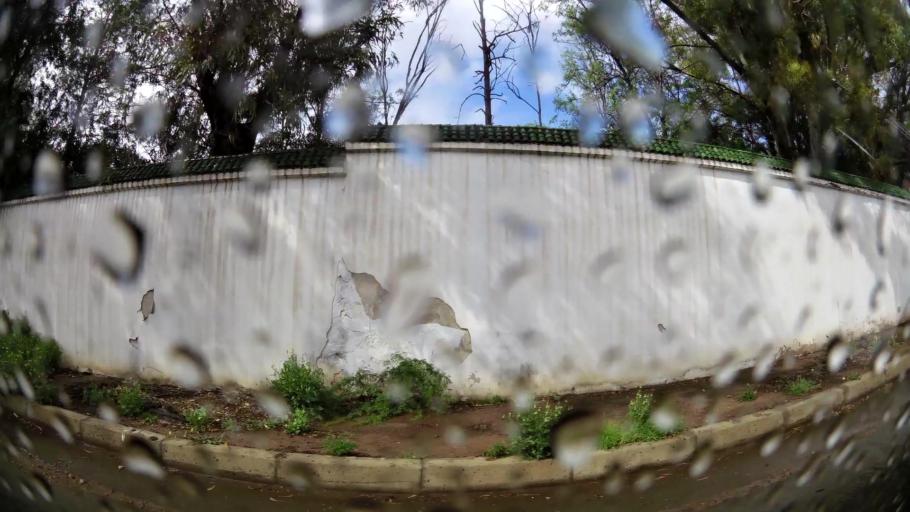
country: MA
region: Grand Casablanca
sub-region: Casablanca
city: Casablanca
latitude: 33.5275
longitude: -7.6287
